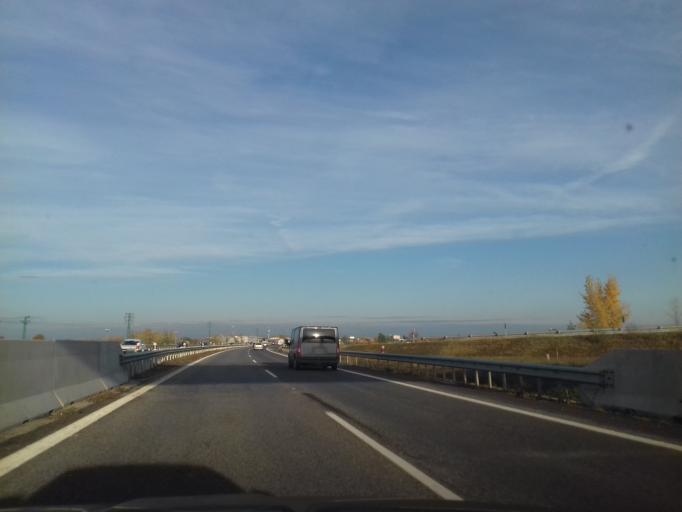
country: SK
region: Trnavsky
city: Sladkovicovo
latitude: 48.3009
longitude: 17.6593
